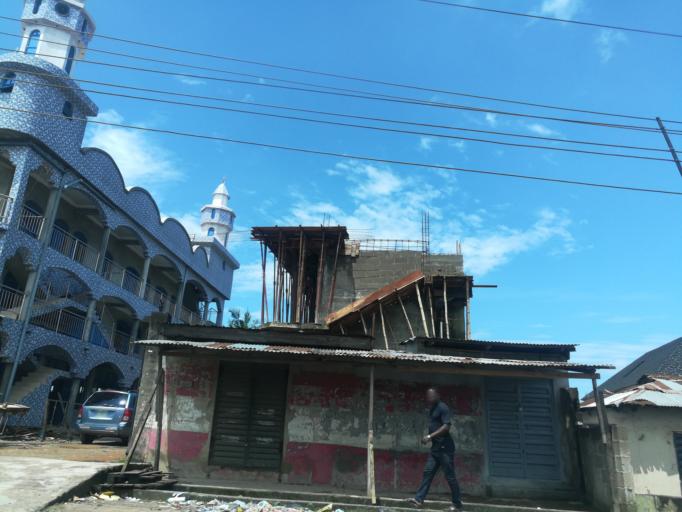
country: NG
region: Lagos
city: Agege
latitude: 6.6204
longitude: 3.3301
